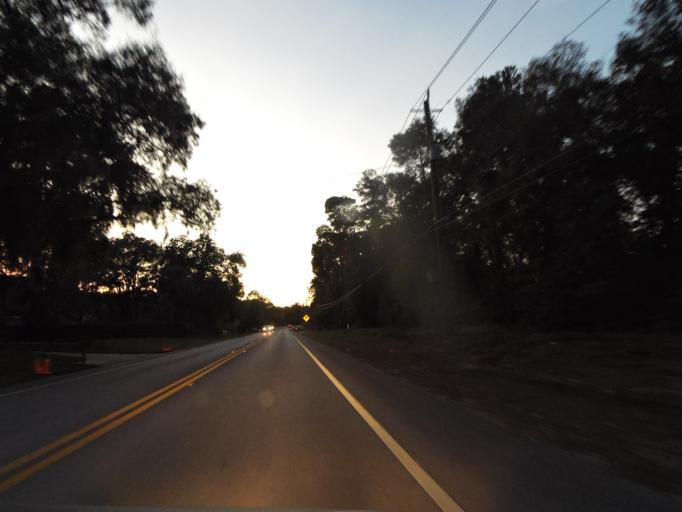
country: US
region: Florida
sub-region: Saint Johns County
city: Saint Augustine Shores
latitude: 29.8148
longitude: -81.3380
